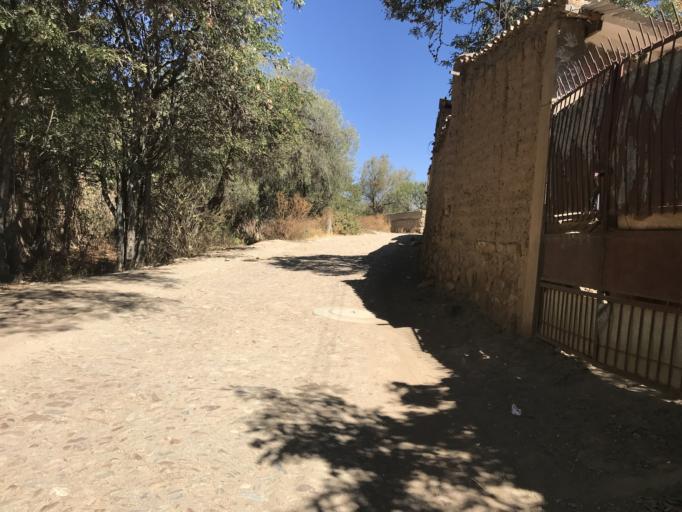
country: BO
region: Cochabamba
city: Tarata
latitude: -17.6166
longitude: -66.0268
